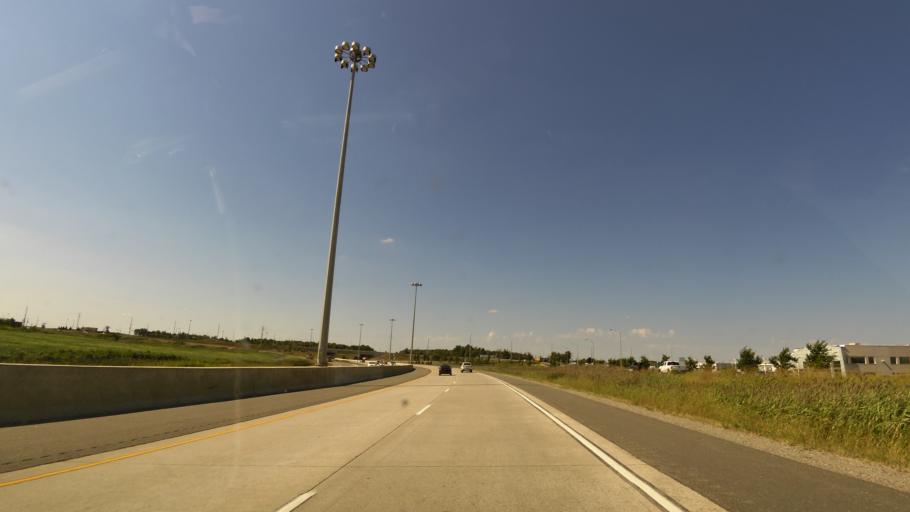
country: CA
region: Ontario
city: Brampton
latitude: 43.7544
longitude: -79.7933
